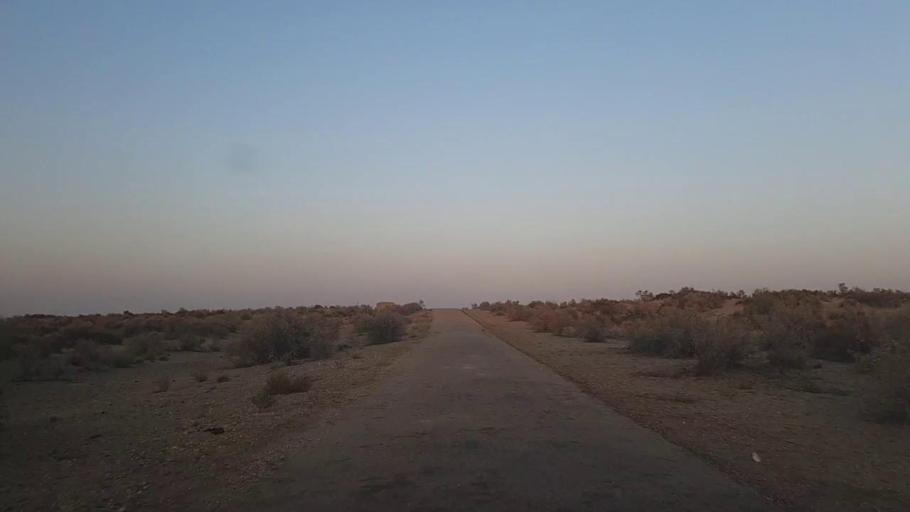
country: PK
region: Sindh
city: Jam Sahib
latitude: 26.3846
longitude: 68.6935
